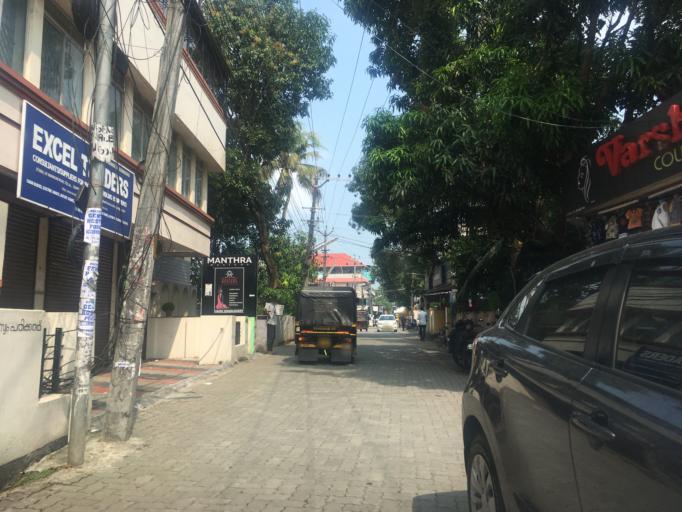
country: IN
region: Kerala
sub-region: Ernakulam
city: Elur
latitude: 10.0303
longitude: 76.3101
